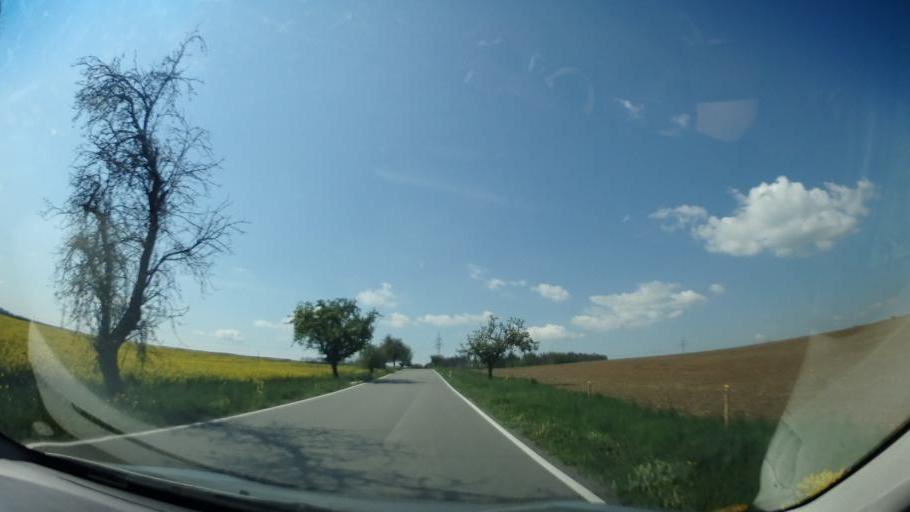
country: CZ
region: Vysocina
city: Namest' nad Oslavou
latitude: 49.1968
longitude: 16.0941
